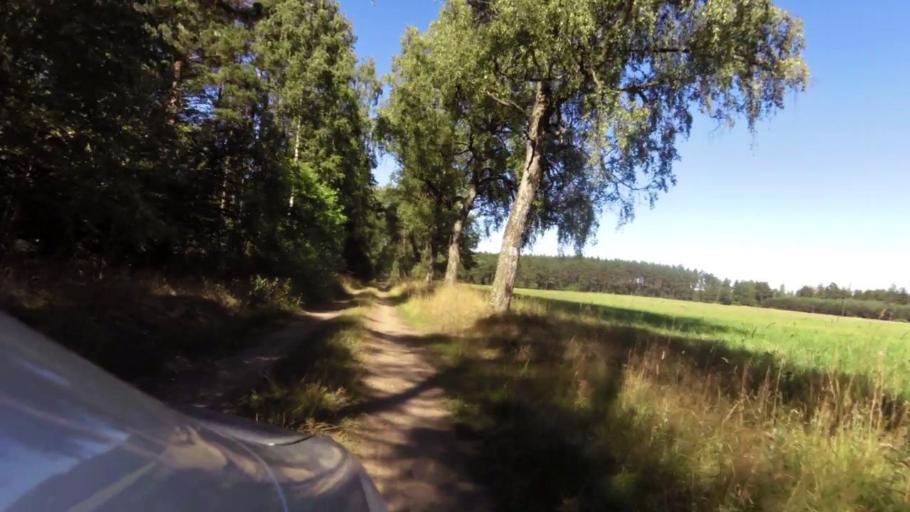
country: PL
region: West Pomeranian Voivodeship
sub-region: Powiat szczecinecki
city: Bialy Bor
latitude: 53.8253
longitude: 16.8672
